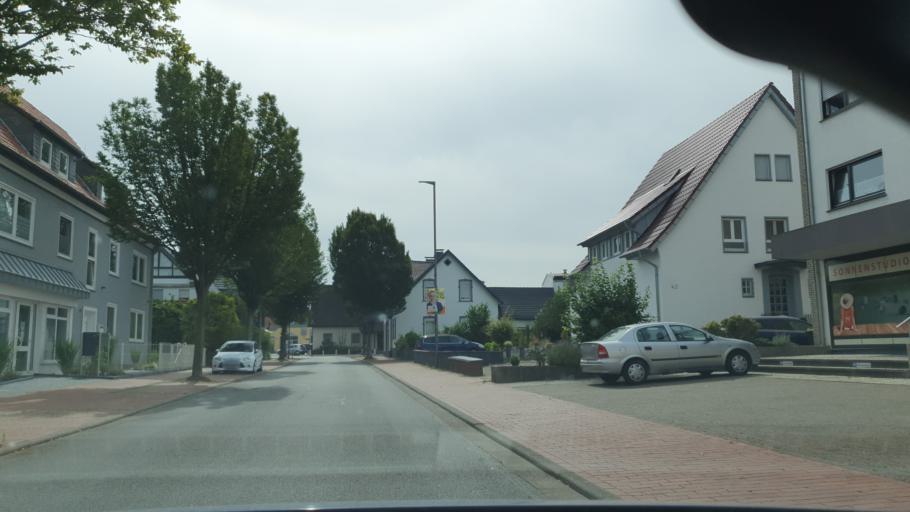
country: DE
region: North Rhine-Westphalia
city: Spenge
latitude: 52.1413
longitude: 8.4882
